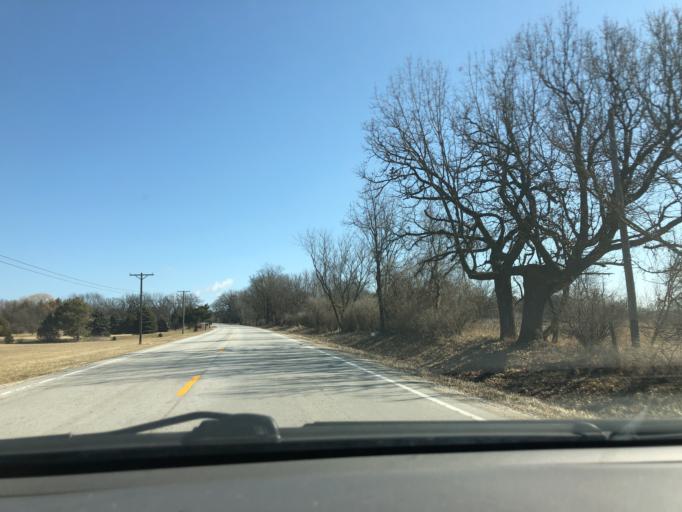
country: US
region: Illinois
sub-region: Kane County
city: Hampshire
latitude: 42.1063
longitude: -88.5066
